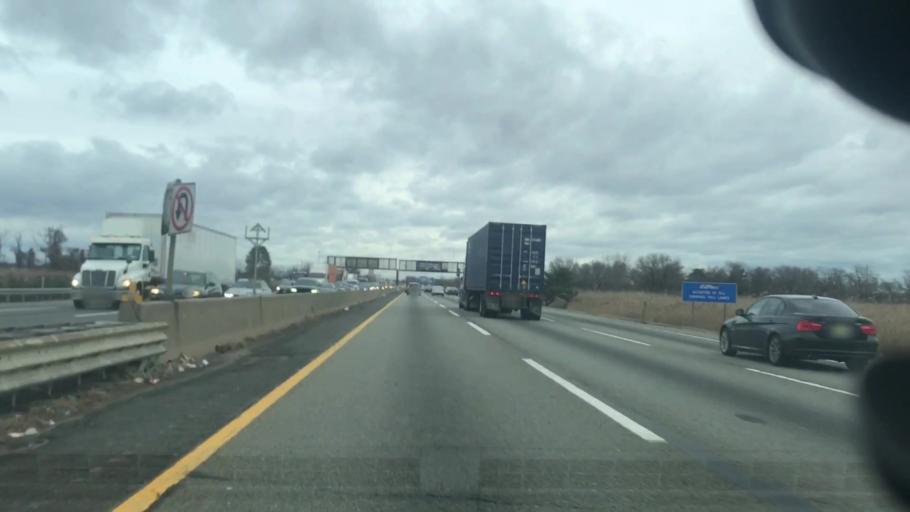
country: US
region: New Jersey
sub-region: Hudson County
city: North Bergen
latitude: 40.8165
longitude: -74.0282
